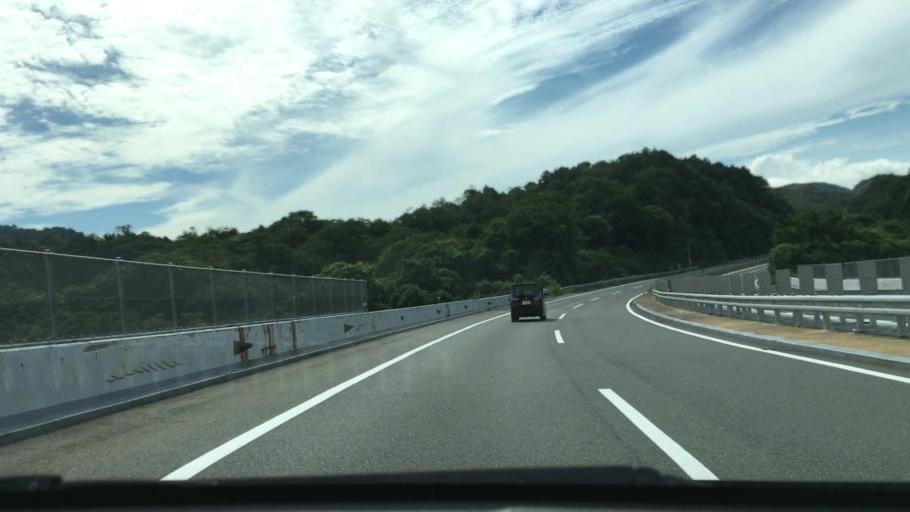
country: JP
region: Yamaguchi
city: Ogori-shimogo
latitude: 34.1267
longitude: 131.3848
